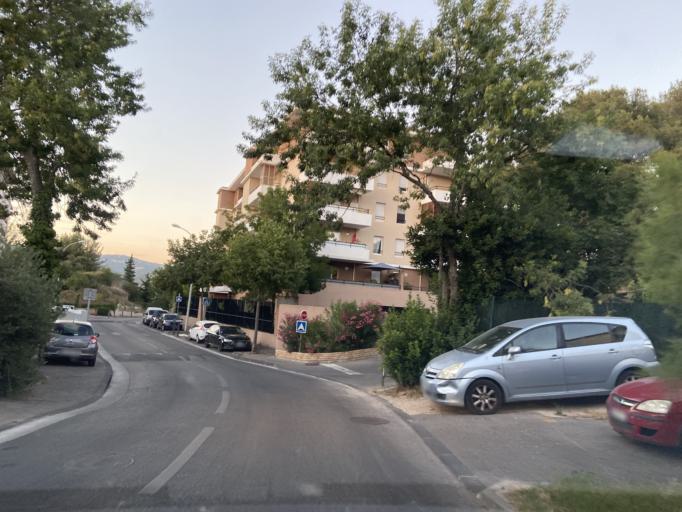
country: FR
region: Provence-Alpes-Cote d'Azur
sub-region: Departement des Bouches-du-Rhone
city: Plan-de-Cuques
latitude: 43.3305
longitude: 5.4497
